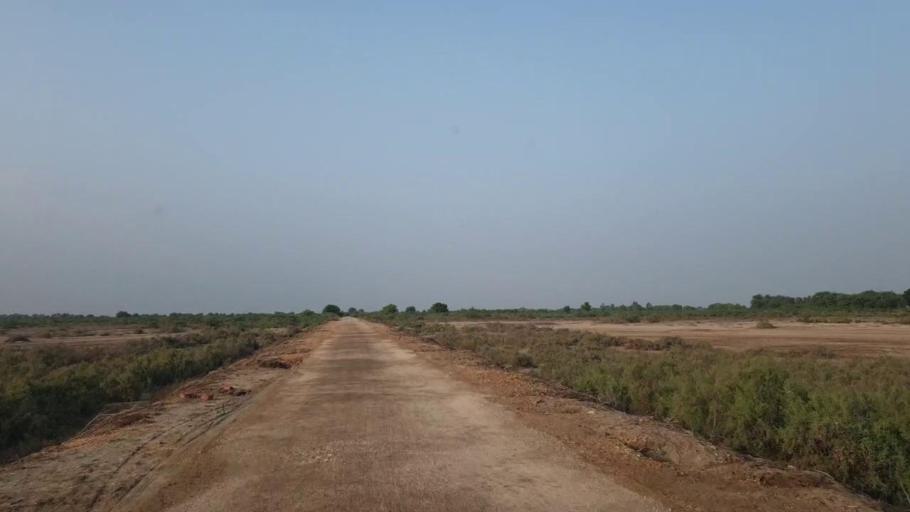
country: PK
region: Sindh
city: Rajo Khanani
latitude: 25.0238
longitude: 68.9773
